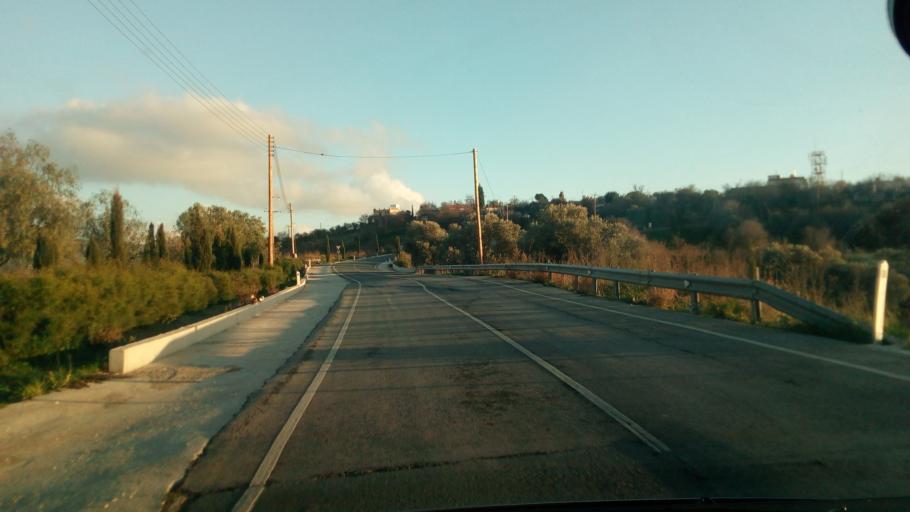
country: CY
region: Pafos
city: Mesogi
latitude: 34.9099
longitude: 32.5493
